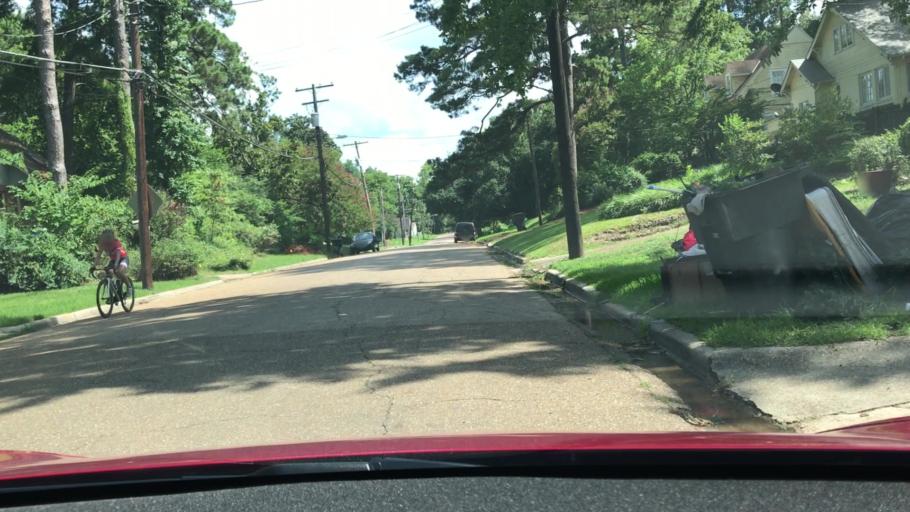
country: US
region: Louisiana
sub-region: Bossier Parish
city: Bossier City
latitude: 32.4794
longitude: -93.7313
